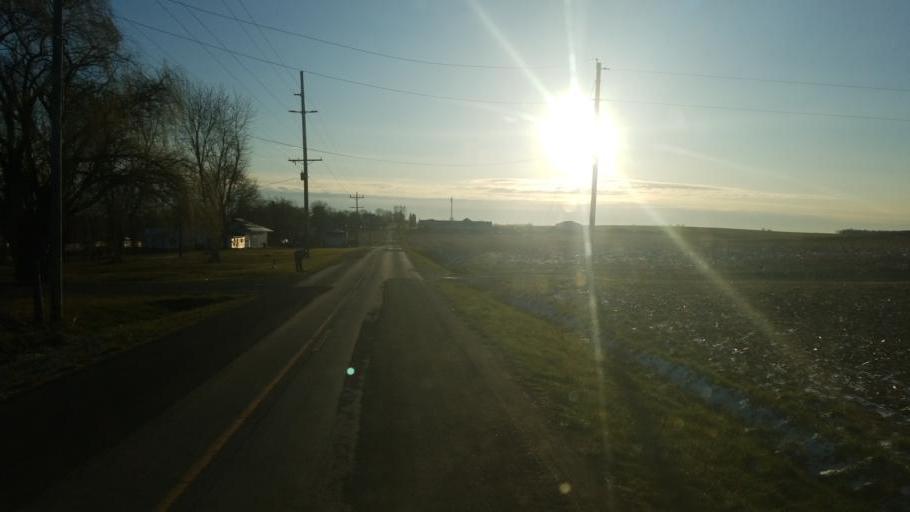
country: US
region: Ohio
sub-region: Highland County
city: Greenfield
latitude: 39.2594
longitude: -83.4556
